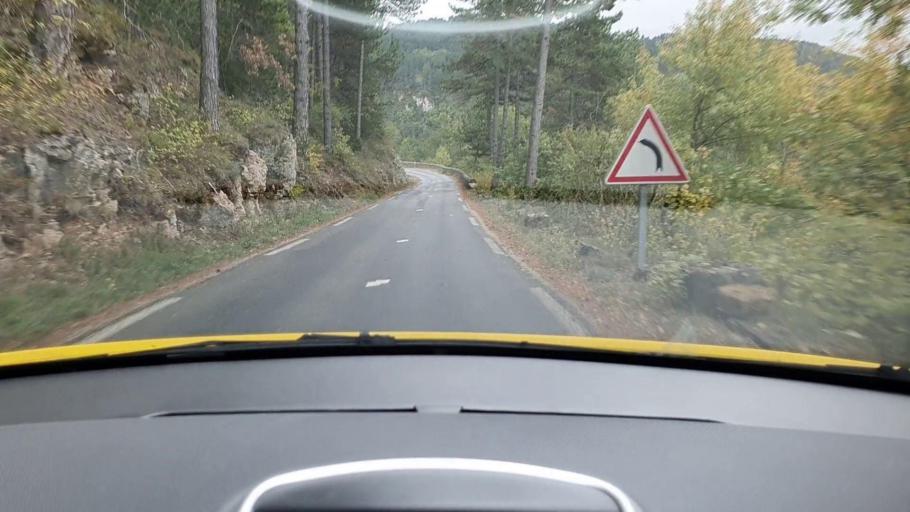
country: FR
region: Languedoc-Roussillon
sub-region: Departement de la Lozere
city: Meyrueis
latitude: 44.0801
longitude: 3.3603
